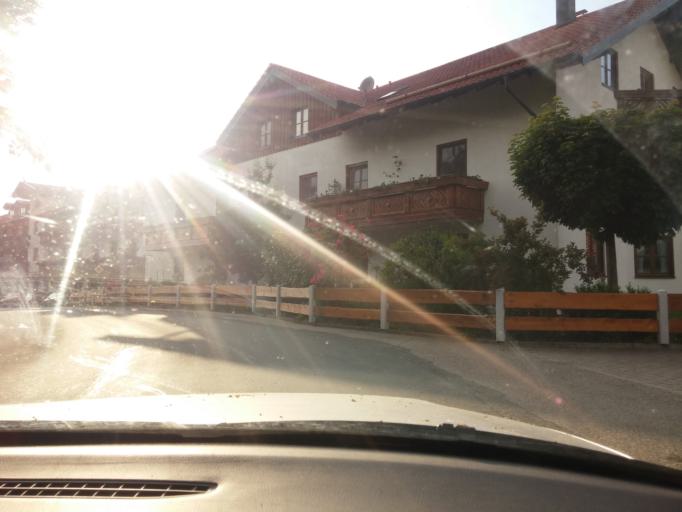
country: DE
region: Bavaria
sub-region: Upper Bavaria
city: Ebersberg
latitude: 48.0786
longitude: 11.9970
